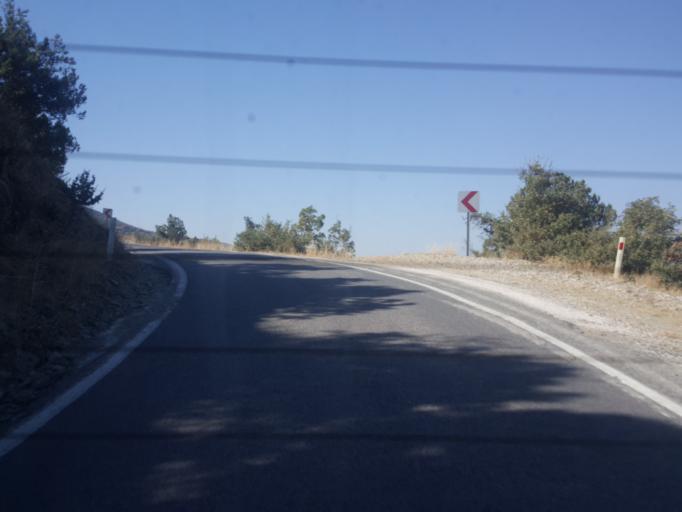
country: TR
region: Kastamonu
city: Tosya
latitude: 40.9914
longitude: 34.1740
